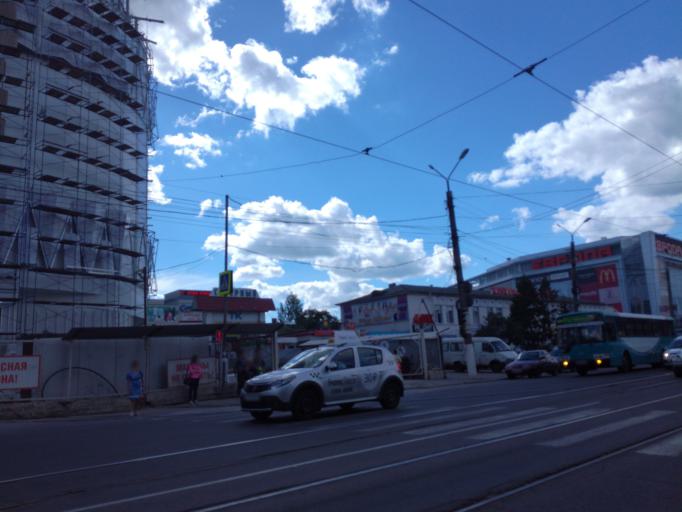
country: RU
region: Kursk
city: Kursk
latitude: 51.7497
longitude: 36.1931
